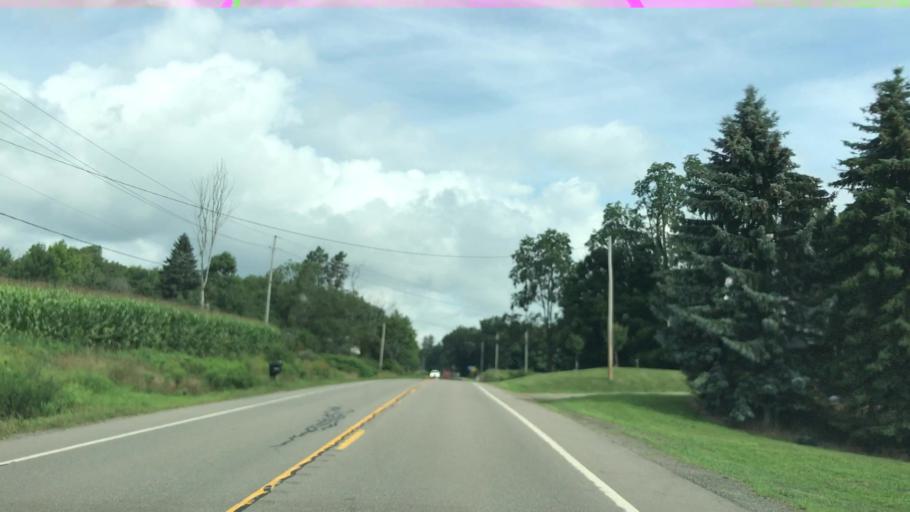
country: US
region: New York
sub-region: Ontario County
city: Naples
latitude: 42.5046
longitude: -77.2859
